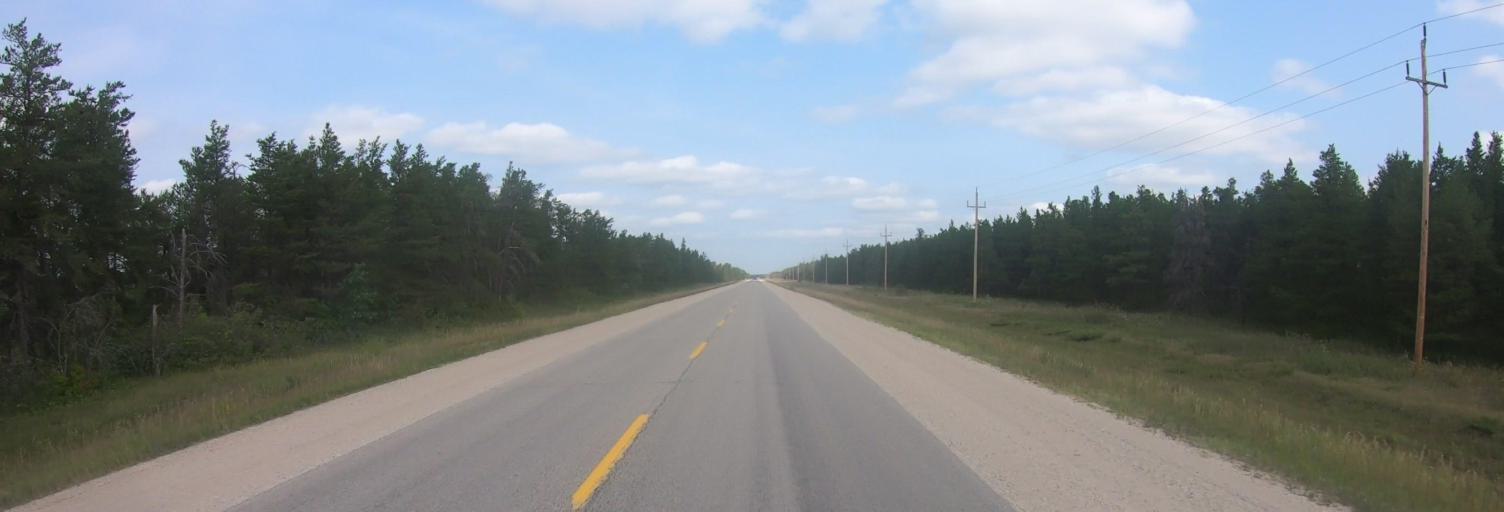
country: CA
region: Manitoba
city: La Broquerie
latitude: 49.2420
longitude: -96.3485
